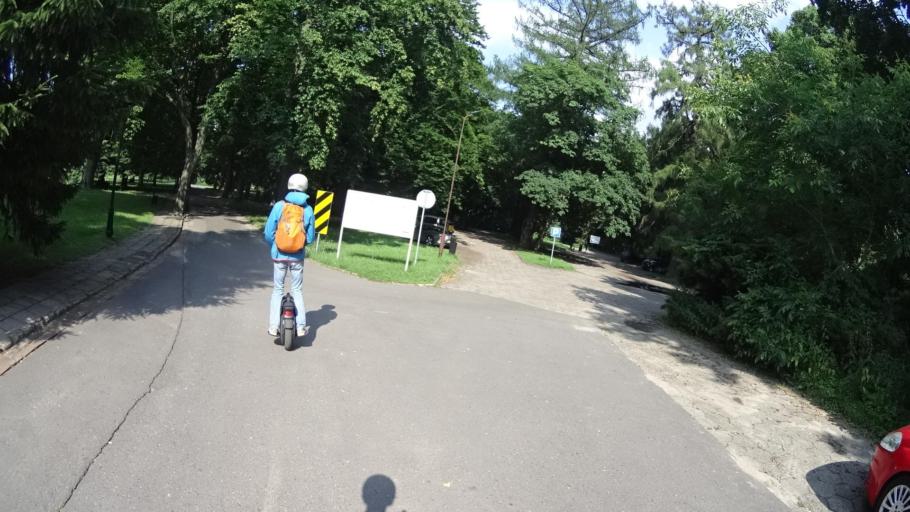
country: PL
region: Masovian Voivodeship
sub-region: Powiat legionowski
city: Jablonna
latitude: 52.3751
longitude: 20.9148
